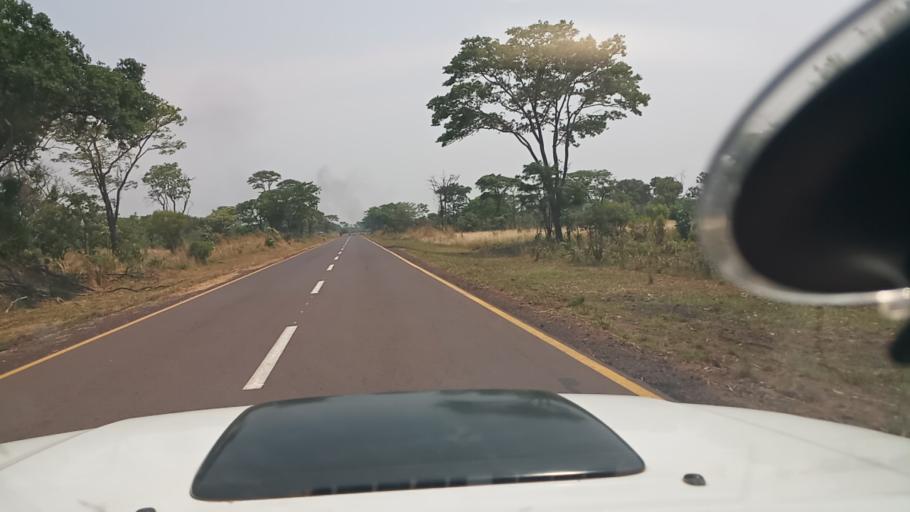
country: ZM
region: Luapula
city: Mwense
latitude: -10.8004
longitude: 28.2323
